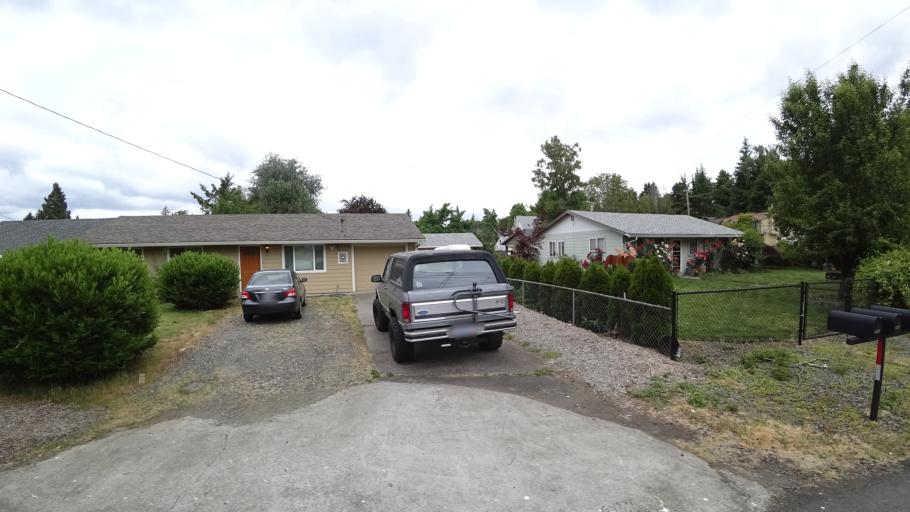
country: US
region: Oregon
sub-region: Multnomah County
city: Lents
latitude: 45.5010
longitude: -122.5695
